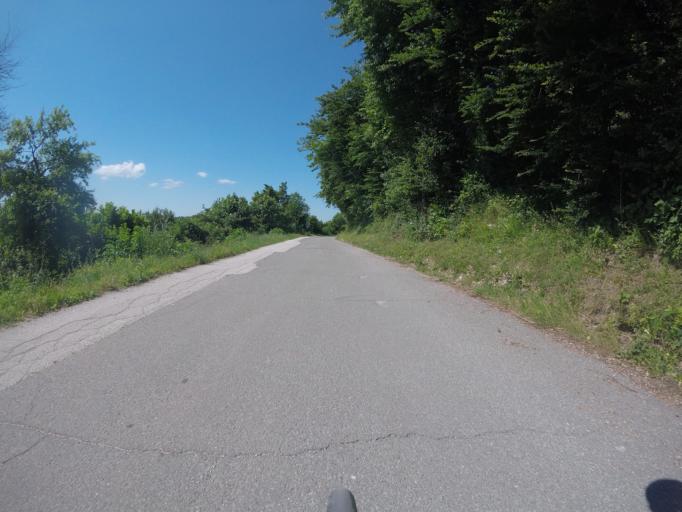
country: SI
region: Kostanjevica na Krki
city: Kostanjevica na Krki
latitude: 45.8101
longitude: 15.5037
